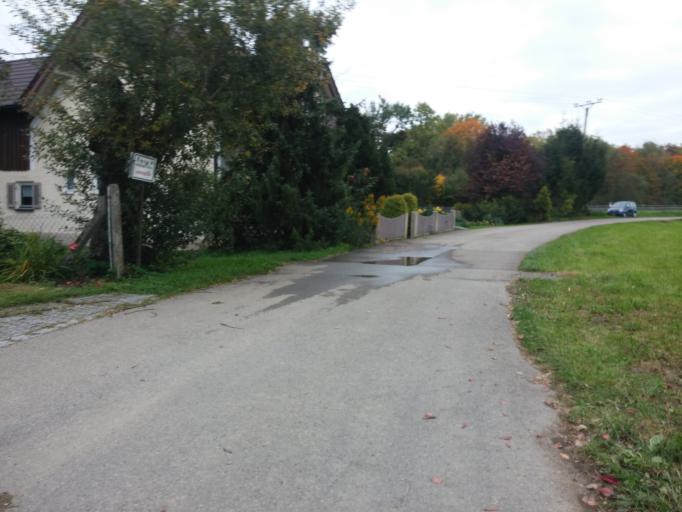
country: DE
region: Baden-Wuerttemberg
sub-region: Tuebingen Region
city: Tannheim
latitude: 47.9706
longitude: 10.0873
